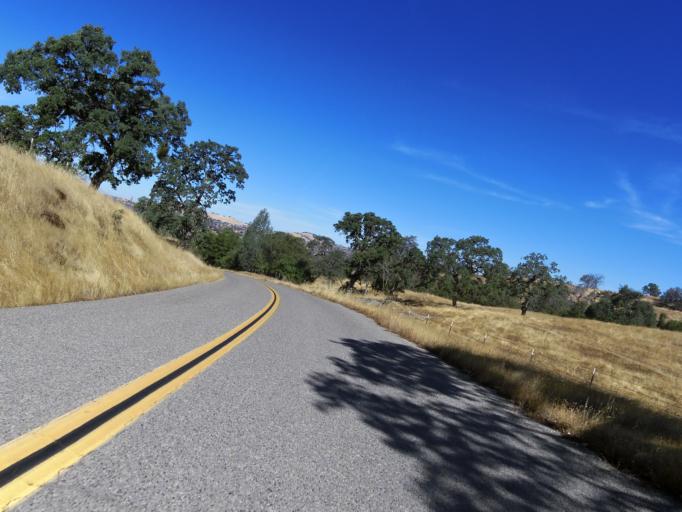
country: US
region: California
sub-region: Madera County
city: Yosemite Lakes
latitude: 37.2638
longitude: -119.9279
